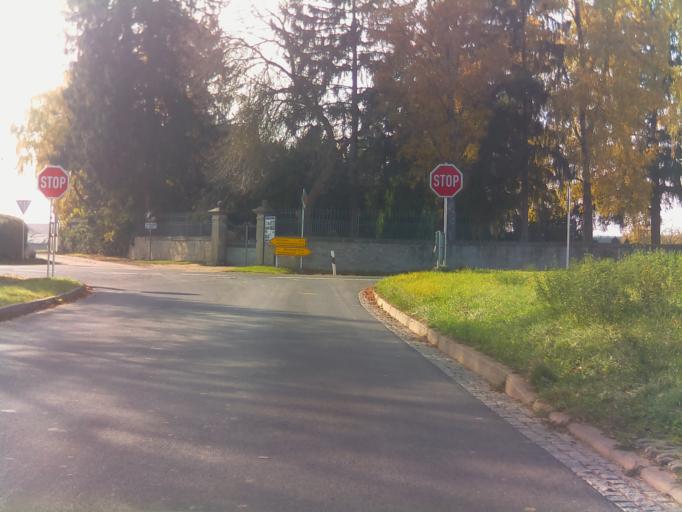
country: DE
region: Bavaria
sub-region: Regierungsbezirk Unterfranken
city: Biebelried
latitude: 49.7458
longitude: 10.0629
